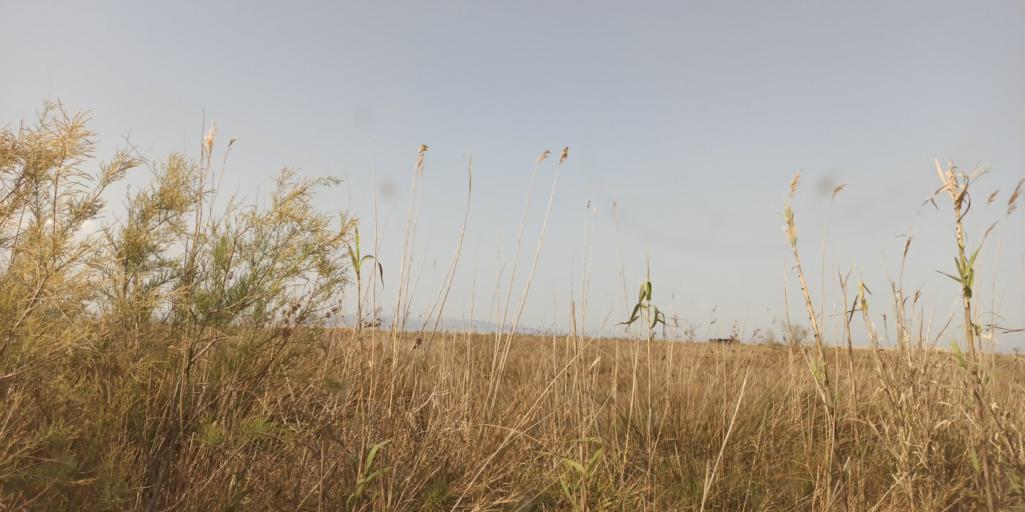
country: ES
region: Catalonia
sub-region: Provincia de Tarragona
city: Deltebre
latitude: 40.7197
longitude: 0.8544
